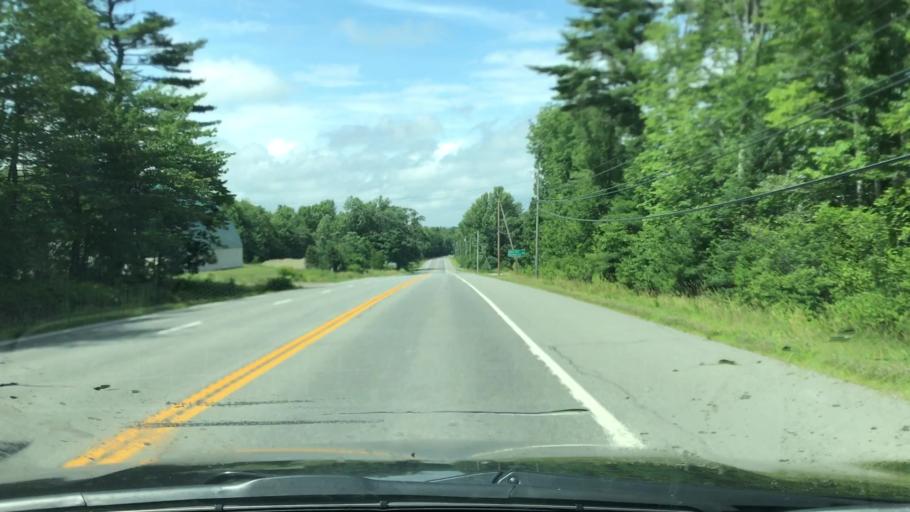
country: US
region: Maine
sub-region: Waldo County
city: Northport
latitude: 44.3661
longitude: -68.9792
